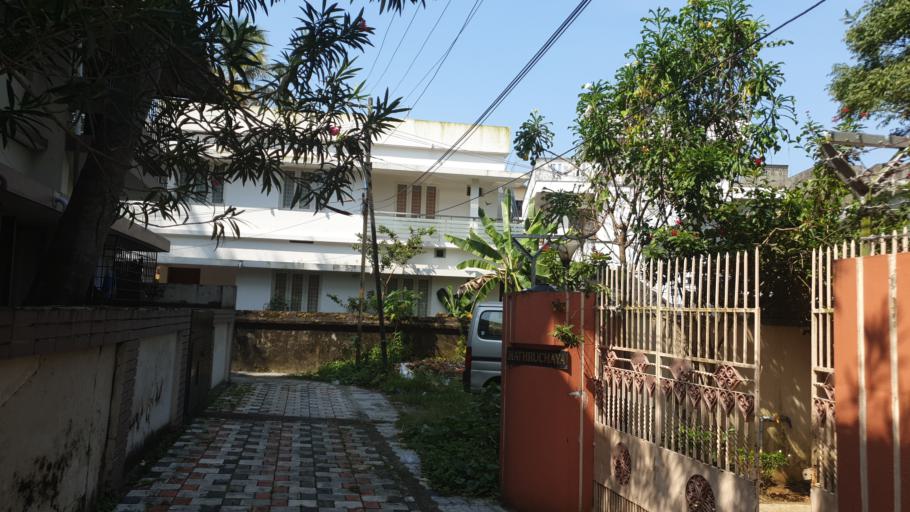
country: IN
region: Kerala
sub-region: Ernakulam
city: Cochin
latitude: 9.9590
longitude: 76.2564
